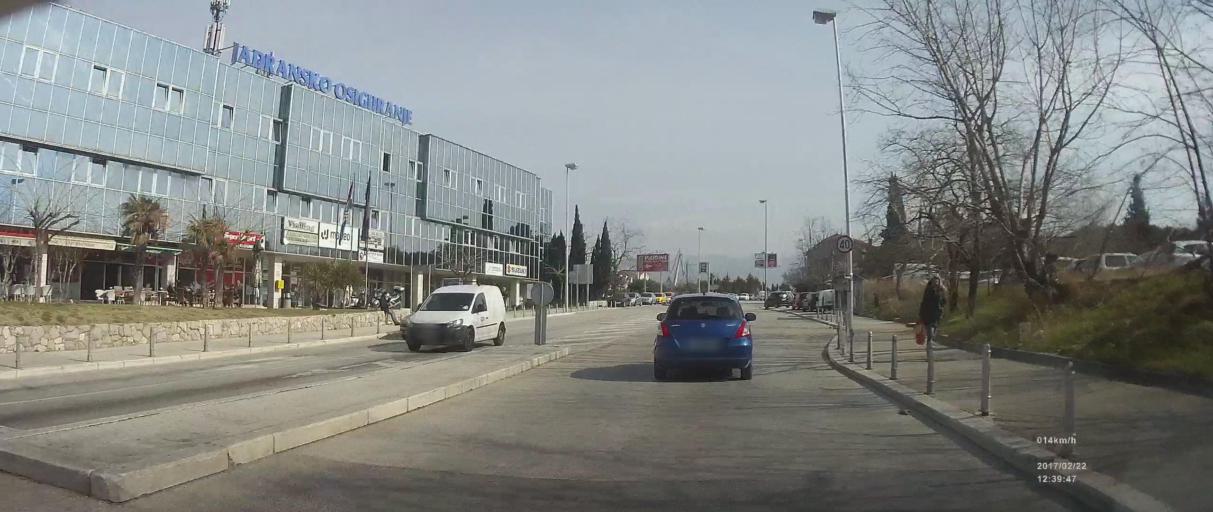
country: HR
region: Splitsko-Dalmatinska
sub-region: Grad Split
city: Split
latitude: 43.5217
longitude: 16.4336
